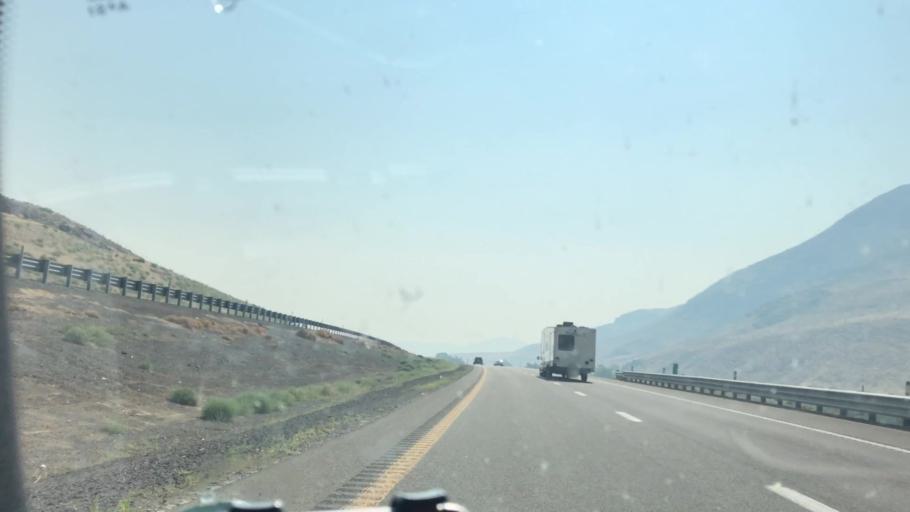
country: US
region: Nevada
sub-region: Lyon County
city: Fernley
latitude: 39.5891
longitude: -119.4444
